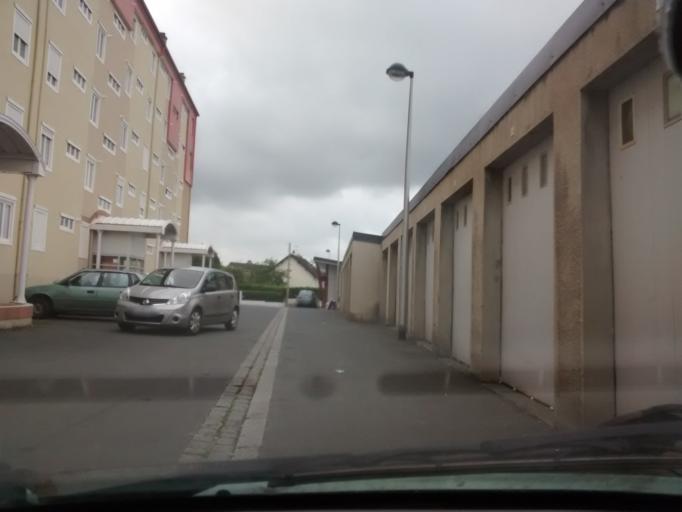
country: FR
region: Lower Normandy
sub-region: Departement de la Manche
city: Saint-Lo
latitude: 49.1097
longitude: -1.0859
